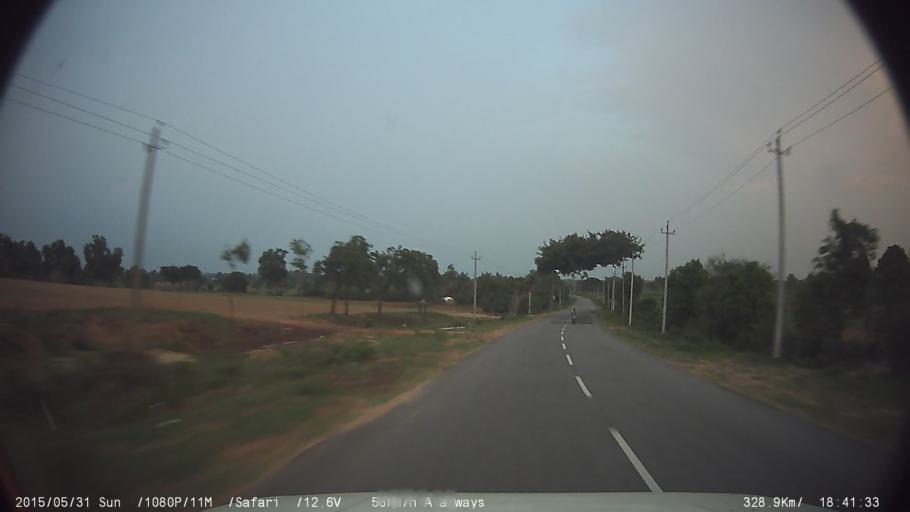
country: IN
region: Karnataka
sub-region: Mysore
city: Nanjangud
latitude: 12.1503
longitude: 76.7936
